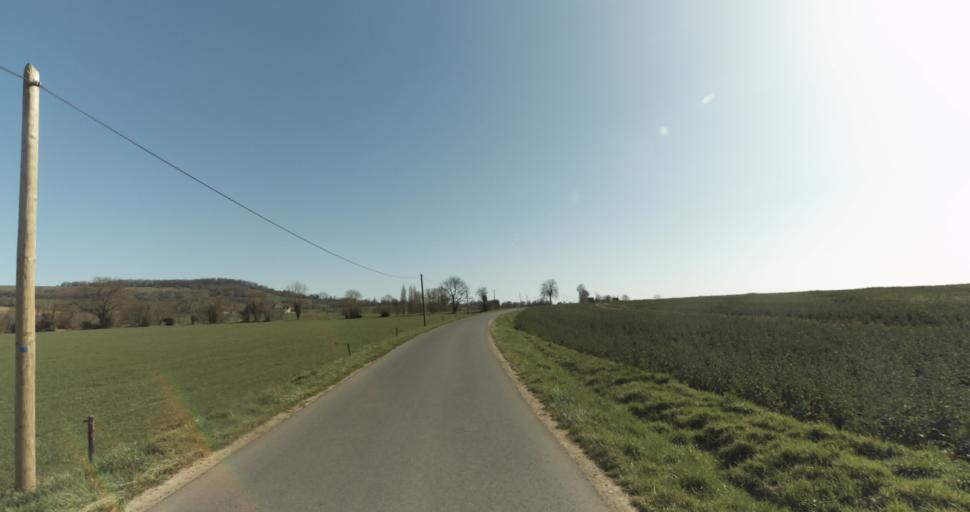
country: FR
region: Lower Normandy
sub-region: Departement de l'Orne
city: Trun
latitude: 48.9084
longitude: 0.0343
